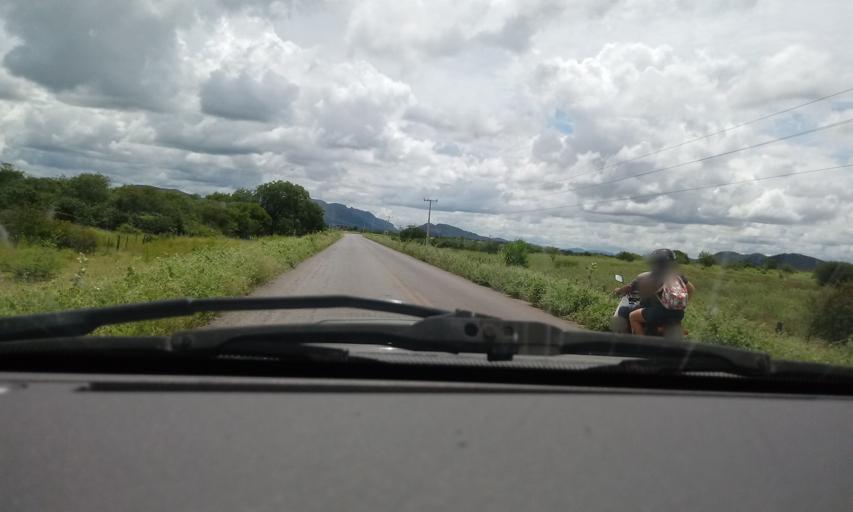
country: BR
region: Bahia
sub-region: Guanambi
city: Guanambi
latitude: -14.1928
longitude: -42.7972
